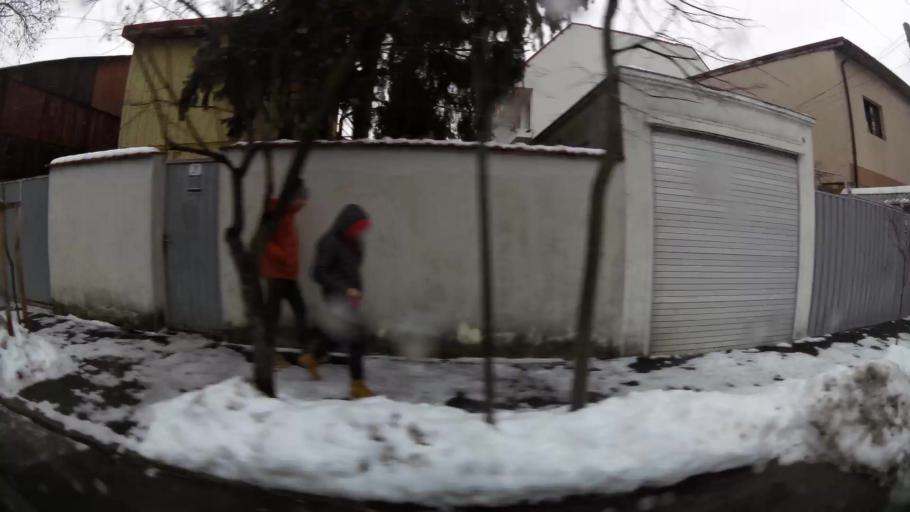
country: RO
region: Ilfov
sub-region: Comuna Chiajna
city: Rosu
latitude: 44.4920
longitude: 26.0362
